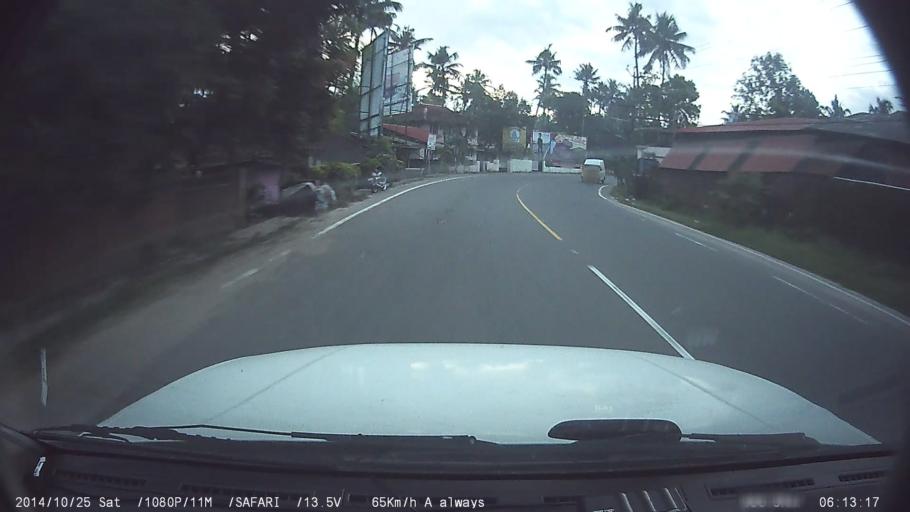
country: IN
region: Kerala
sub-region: Ernakulam
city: Perumpavur
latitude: 10.1458
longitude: 76.4603
